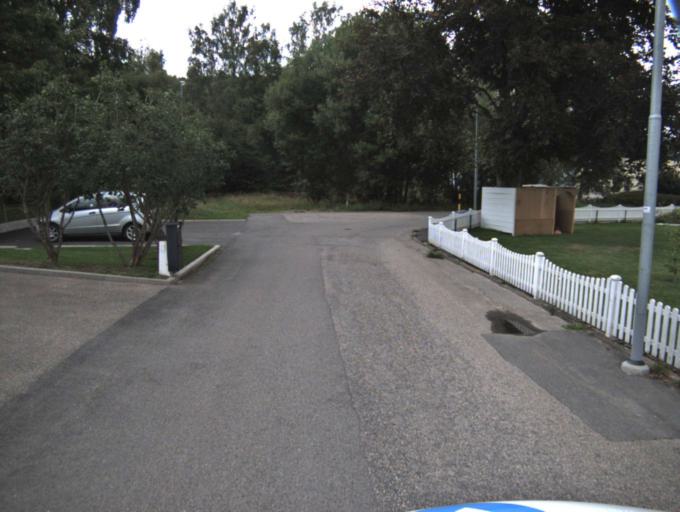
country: SE
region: Vaestra Goetaland
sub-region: Ulricehamns Kommun
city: Ulricehamn
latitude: 57.8057
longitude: 13.4045
